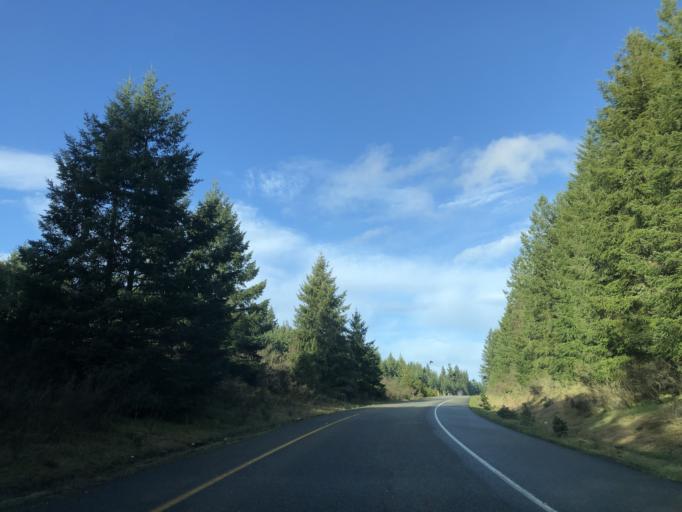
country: US
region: Washington
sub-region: Kitsap County
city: Bangor Trident Base
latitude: 47.7027
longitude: -122.6836
